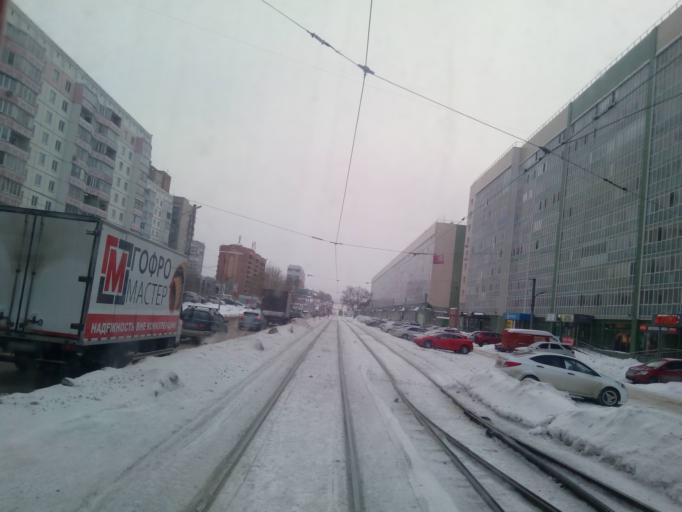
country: RU
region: Novosibirsk
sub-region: Novosibirskiy Rayon
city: Novosibirsk
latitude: 54.9915
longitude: 82.8569
